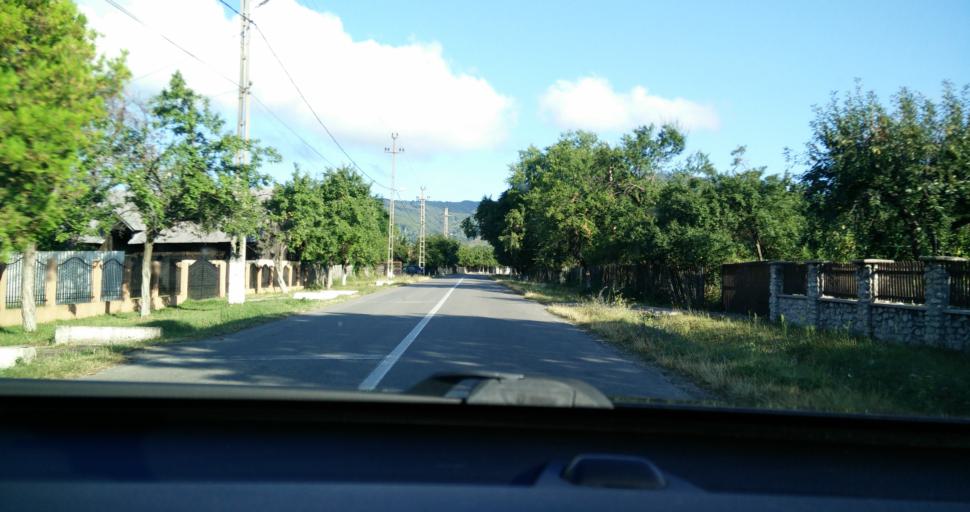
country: RO
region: Gorj
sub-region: Comuna Polovragi
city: Polovragi
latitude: 45.1774
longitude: 23.7969
